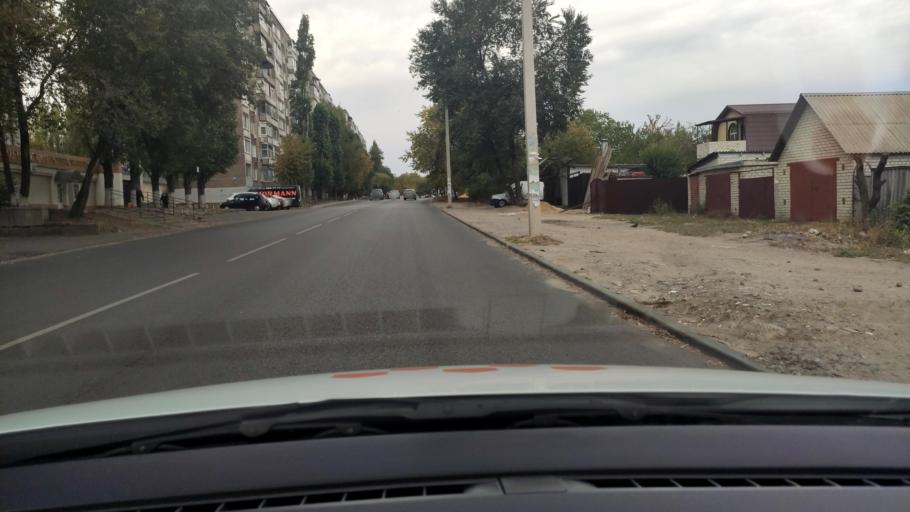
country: RU
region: Voronezj
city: Podgornoye
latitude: 51.6970
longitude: 39.1488
